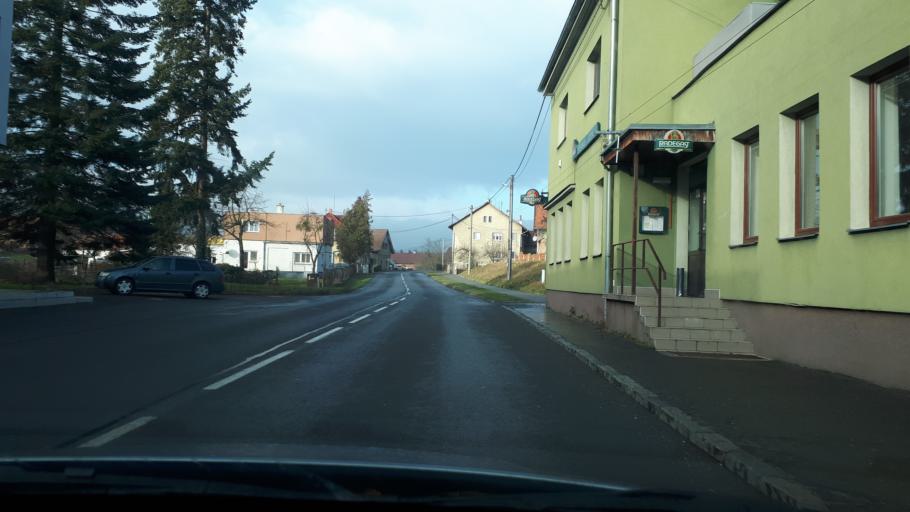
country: CZ
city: Jesenik nad Odrou
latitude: 49.6478
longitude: 17.9348
